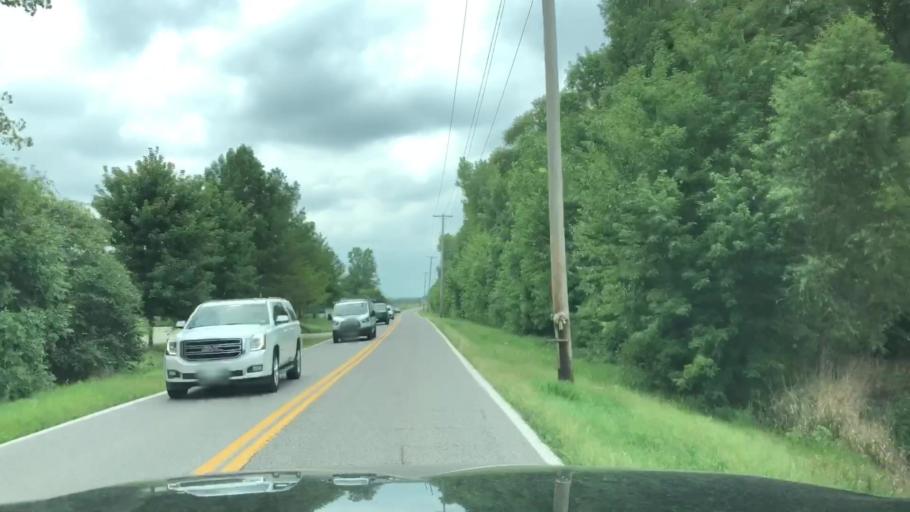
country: US
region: Missouri
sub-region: Saint Louis County
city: Bridgeton
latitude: 38.8054
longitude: -90.4036
